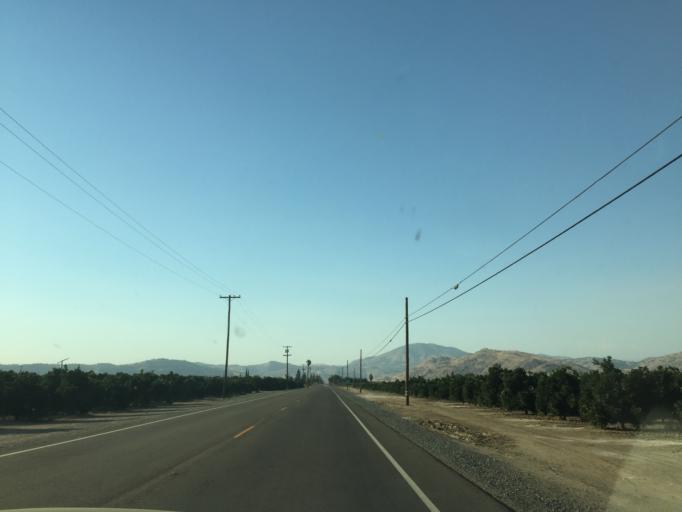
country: US
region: California
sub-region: Fresno County
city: Orange Cove
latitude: 36.6353
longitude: -119.3048
